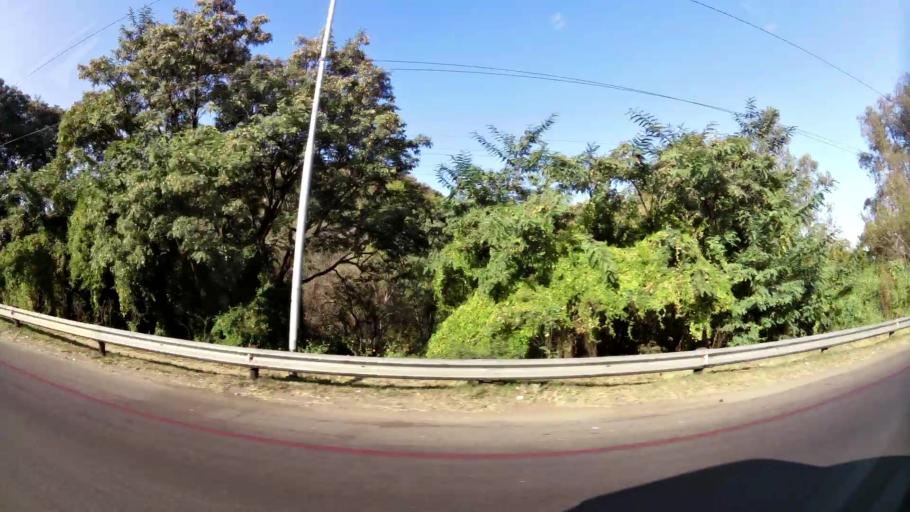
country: ZA
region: Gauteng
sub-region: City of Tshwane Metropolitan Municipality
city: Pretoria
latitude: -25.7296
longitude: 28.1691
